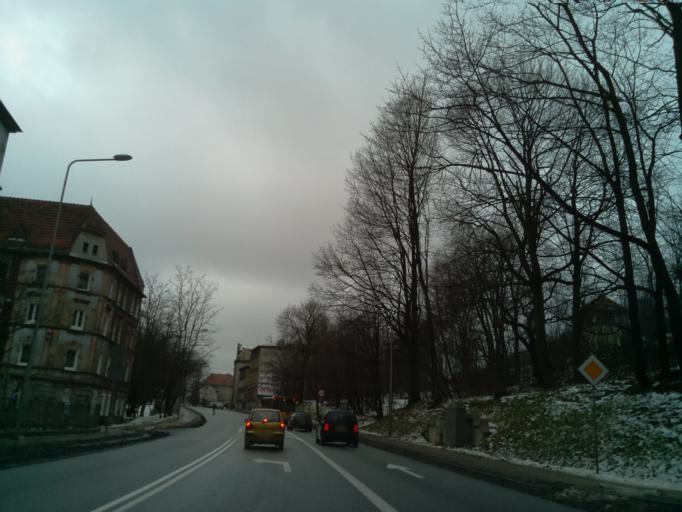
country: PL
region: Lower Silesian Voivodeship
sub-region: Powiat walbrzyski
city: Walbrzych
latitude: 50.7925
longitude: 16.2874
